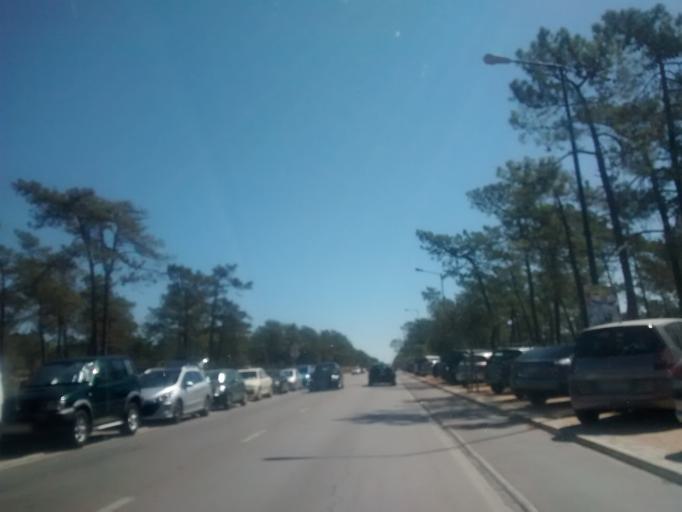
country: PT
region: Faro
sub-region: Vila Real de Santo Antonio
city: Monte Gordo
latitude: 37.1800
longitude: -7.4407
